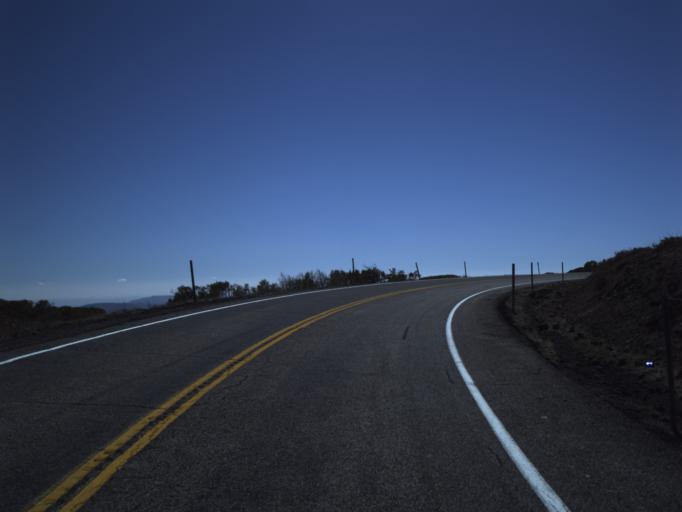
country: US
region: Utah
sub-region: Wayne County
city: Loa
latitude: 38.0449
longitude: -111.3269
